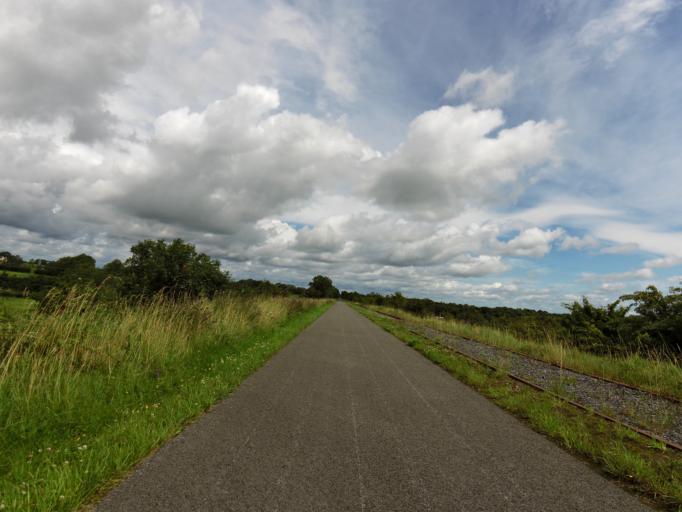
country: IE
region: Leinster
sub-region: An Iarmhi
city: Kilbeggan
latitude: 53.4704
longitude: -7.4928
